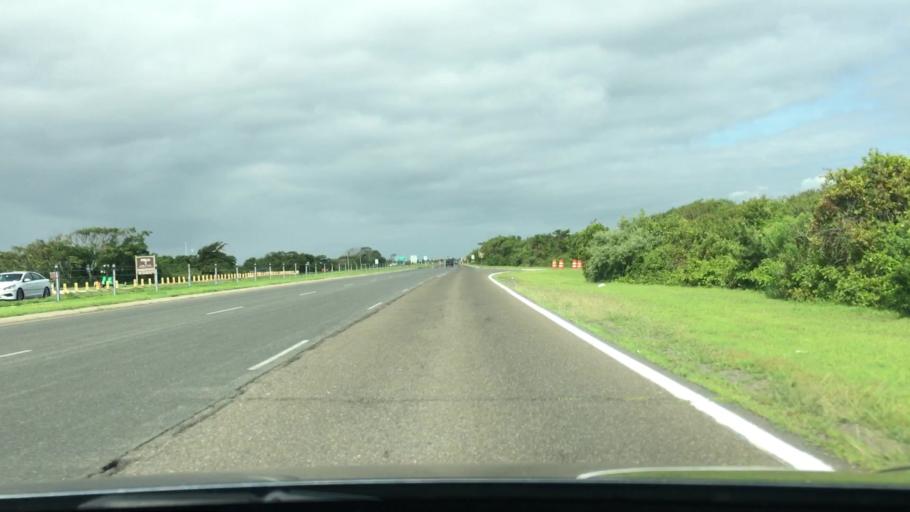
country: US
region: New York
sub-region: Nassau County
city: Point Lookout
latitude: 40.5953
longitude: -73.5203
